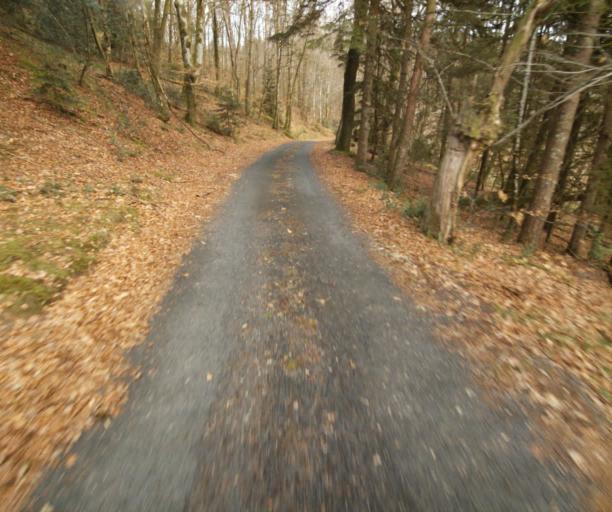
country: FR
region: Limousin
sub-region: Departement de la Correze
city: Correze
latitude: 45.3909
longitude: 1.8859
